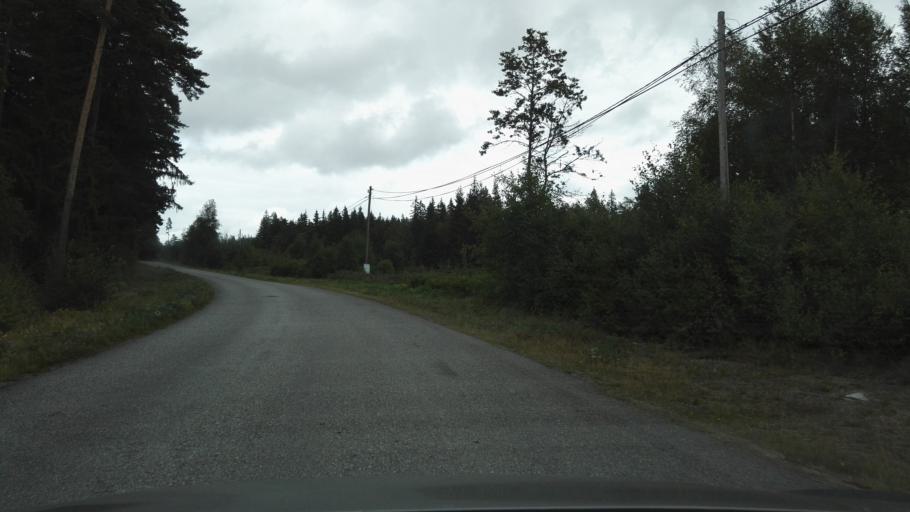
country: SE
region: Joenkoeping
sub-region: Vetlanda Kommun
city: Landsbro
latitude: 57.2954
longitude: 14.8467
